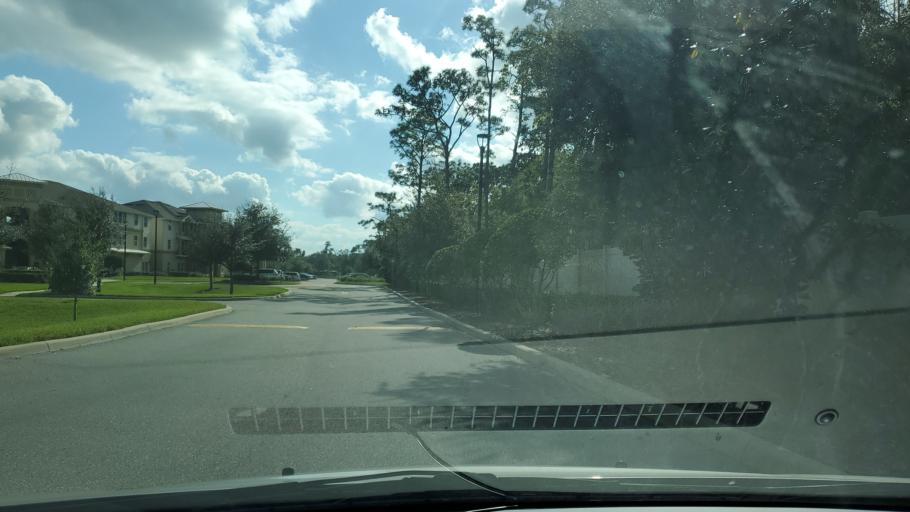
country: US
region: Florida
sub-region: Orange County
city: Conway
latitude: 28.4984
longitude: -81.2967
